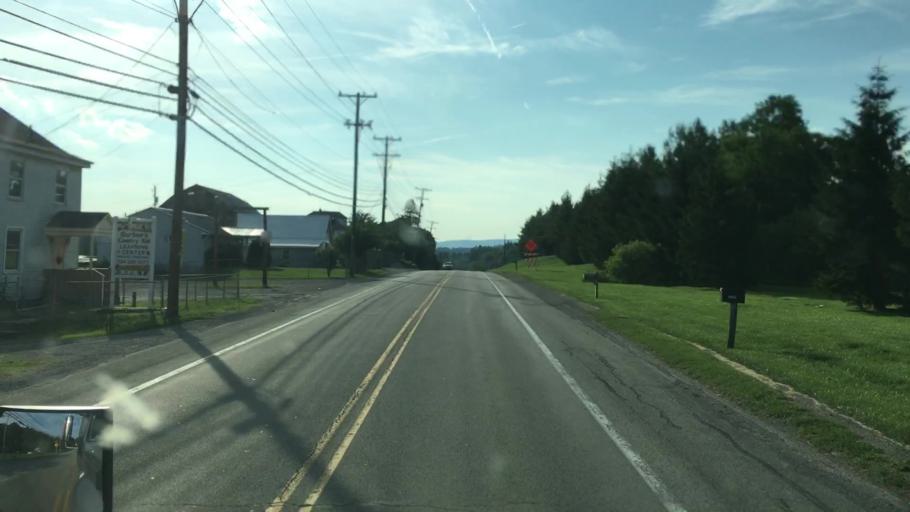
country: US
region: Pennsylvania
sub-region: Fayette County
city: Hopwood
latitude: 39.7971
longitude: -79.5444
